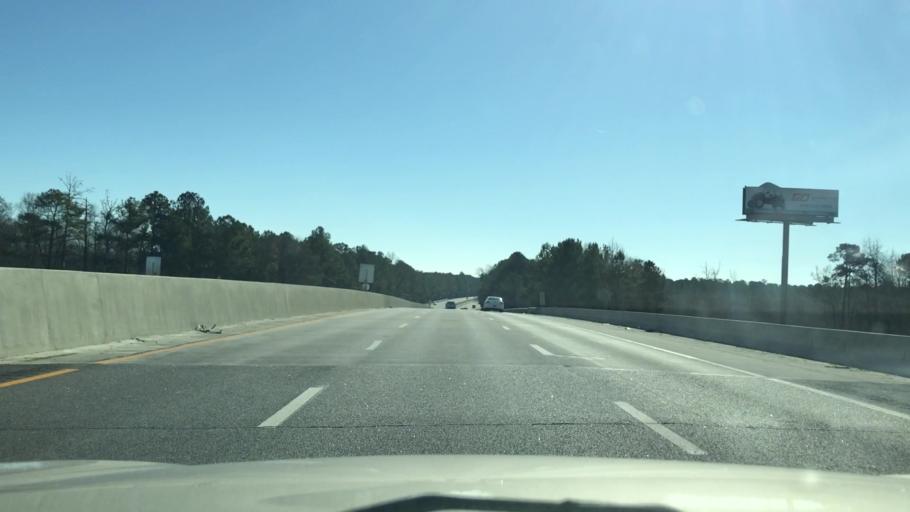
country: US
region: South Carolina
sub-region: Lexington County
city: Pineridge
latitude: 33.9164
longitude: -81.0620
